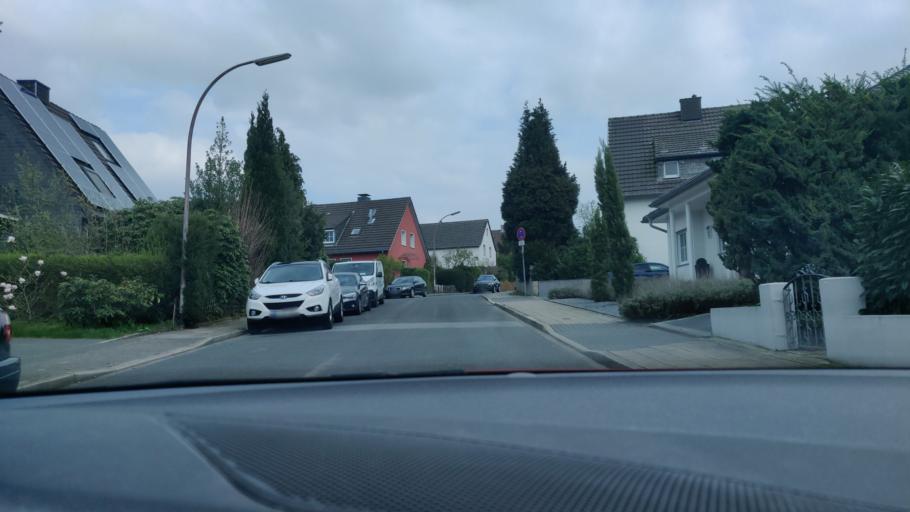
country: DE
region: North Rhine-Westphalia
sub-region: Regierungsbezirk Dusseldorf
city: Velbert
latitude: 51.3261
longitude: 7.0452
